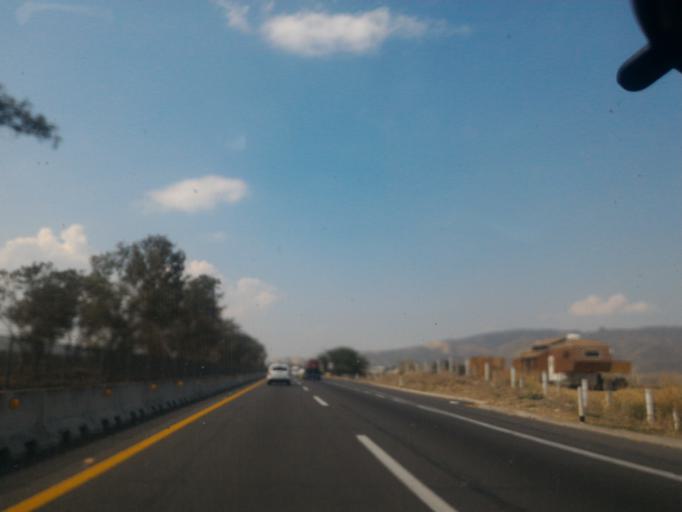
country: MX
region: Jalisco
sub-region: Zapotlan el Grande
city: Ciudad Guzman [CERESO]
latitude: 19.6262
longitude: -103.4643
